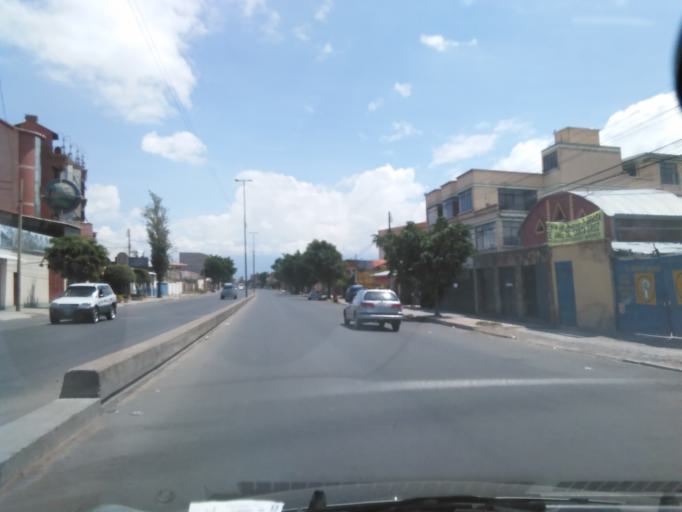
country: BO
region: Cochabamba
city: Cochabamba
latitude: -17.4104
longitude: -66.1648
